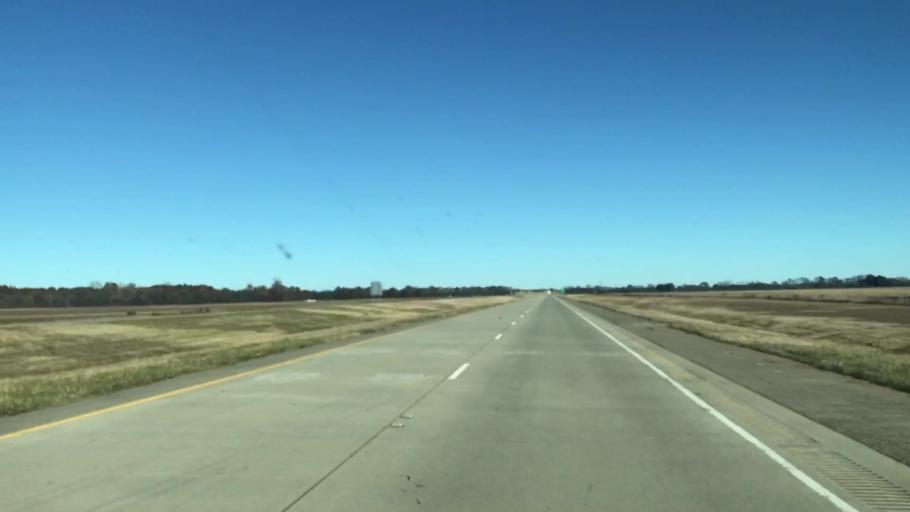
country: US
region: Louisiana
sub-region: Caddo Parish
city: Vivian
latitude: 32.8685
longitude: -93.8601
